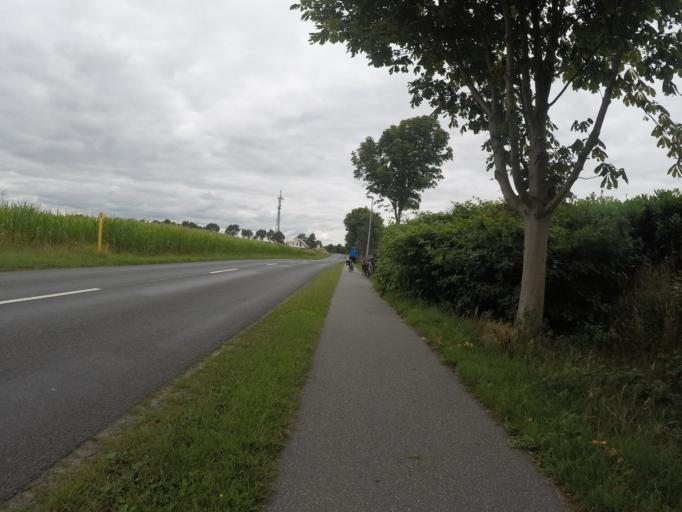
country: DE
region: Lower Saxony
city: Hemmoor
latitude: 53.6916
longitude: 9.1444
